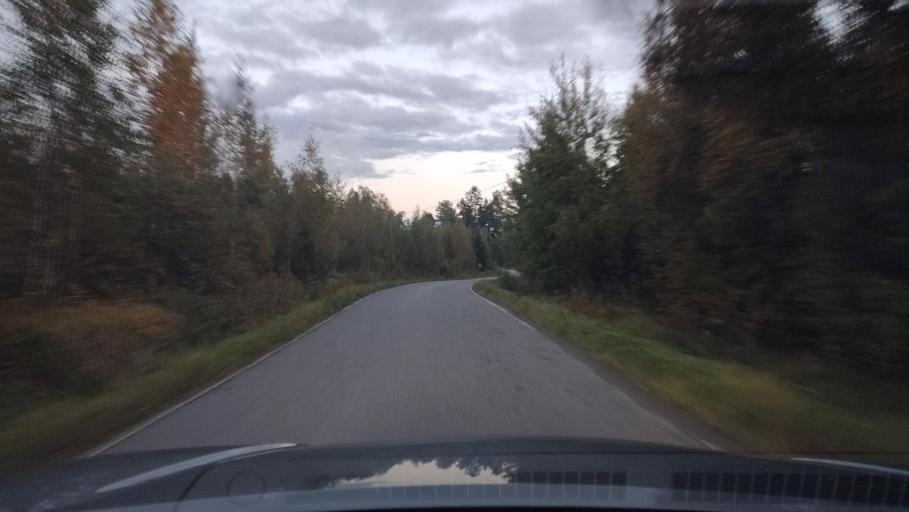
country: FI
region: Ostrobothnia
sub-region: Sydosterbotten
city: Kristinestad
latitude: 62.2757
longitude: 21.5159
